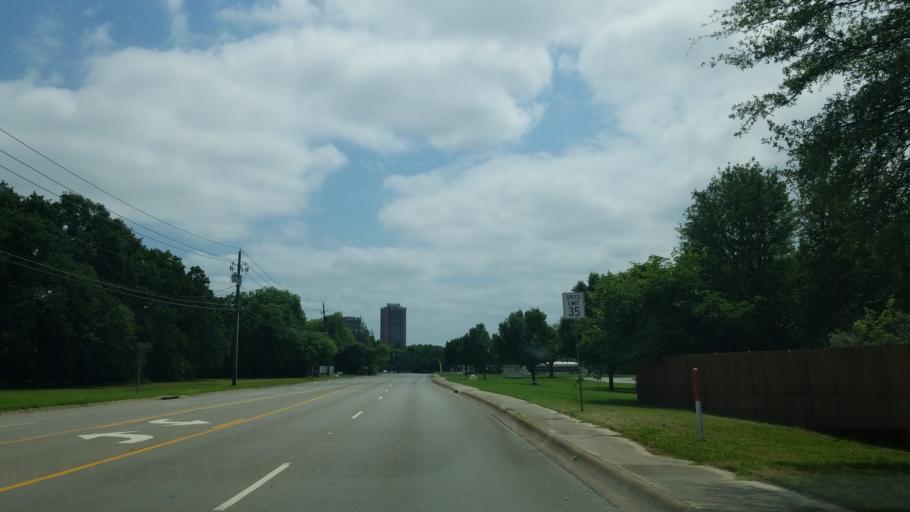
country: US
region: Texas
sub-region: Denton County
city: Denton
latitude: 33.2383
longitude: -97.1232
